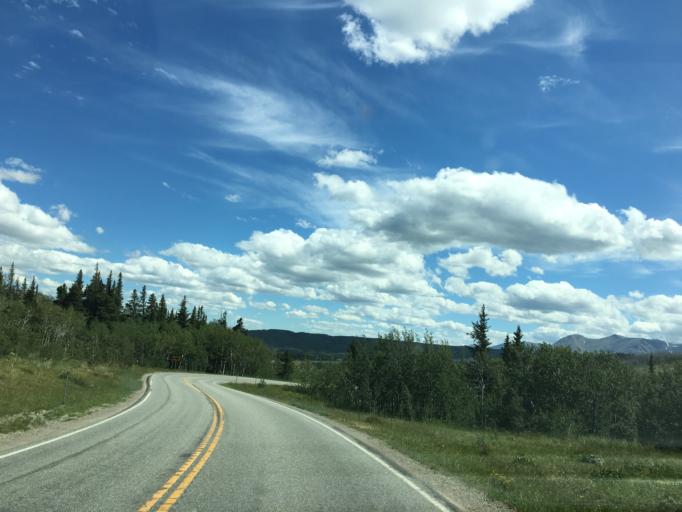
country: US
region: Montana
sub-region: Glacier County
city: North Browning
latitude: 48.6824
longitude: -113.3579
